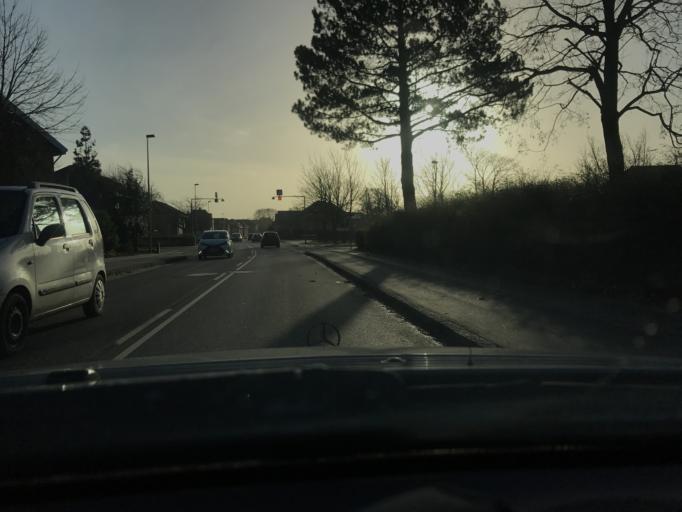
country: DK
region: South Denmark
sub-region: Sonderborg Kommune
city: Sonderborg
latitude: 54.9171
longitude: 9.7875
